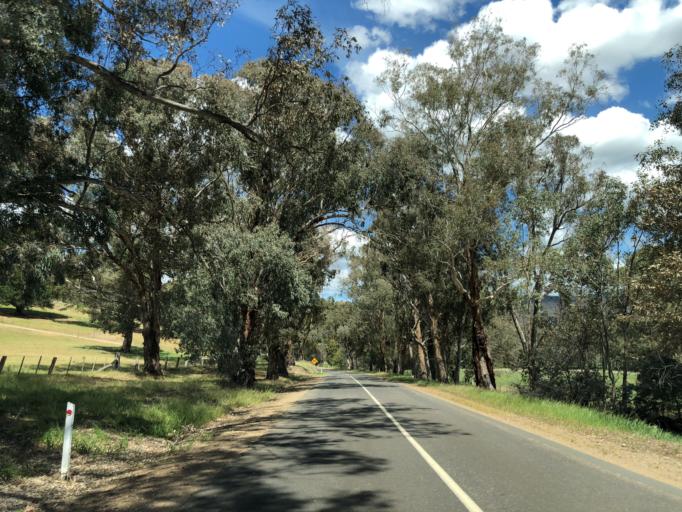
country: AU
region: Victoria
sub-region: Benalla
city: Benalla
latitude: -36.7504
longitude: 146.1186
